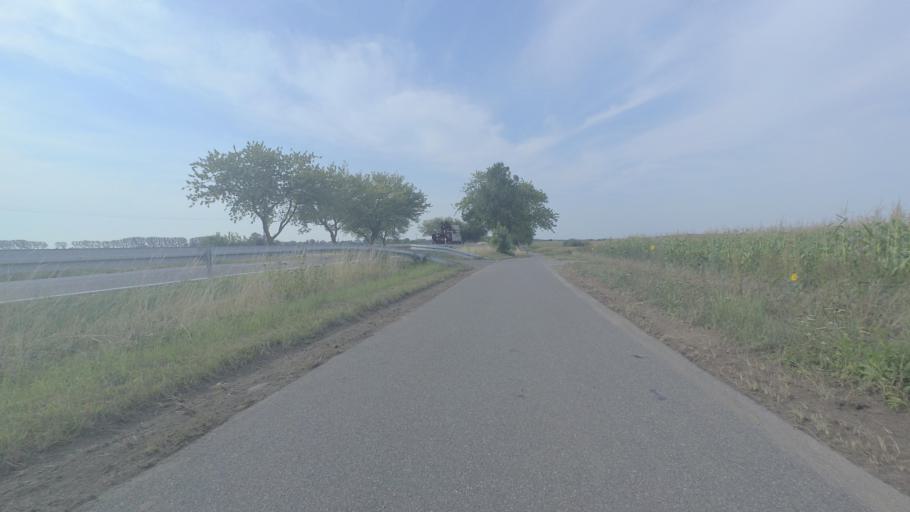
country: DE
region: Mecklenburg-Vorpommern
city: Wackerow
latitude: 53.6724
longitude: 12.9052
